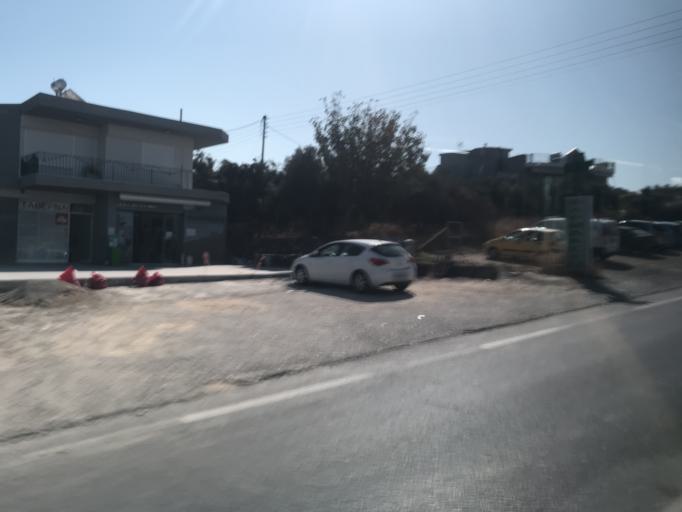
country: GR
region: Crete
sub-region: Nomos Irakleiou
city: Gazi
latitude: 35.3114
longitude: 25.0912
